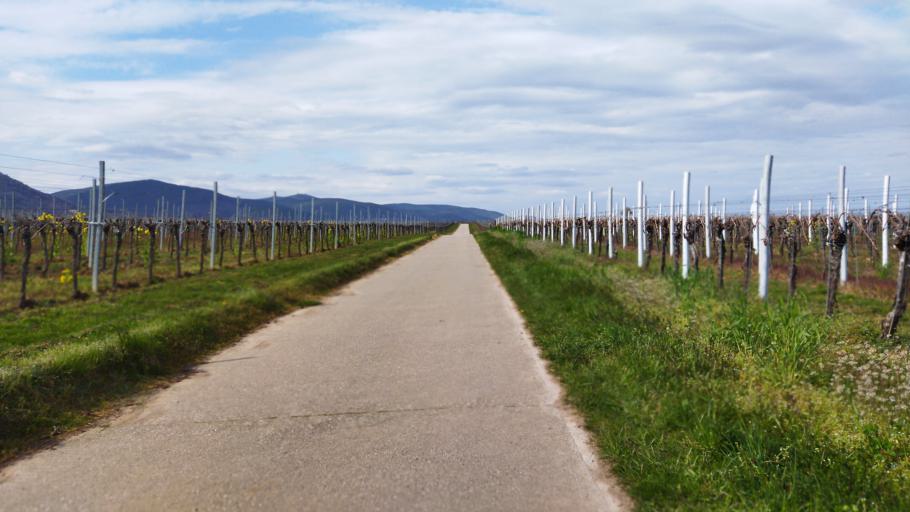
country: DE
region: Rheinland-Pfalz
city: Roschbach
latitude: 49.2498
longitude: 8.1141
